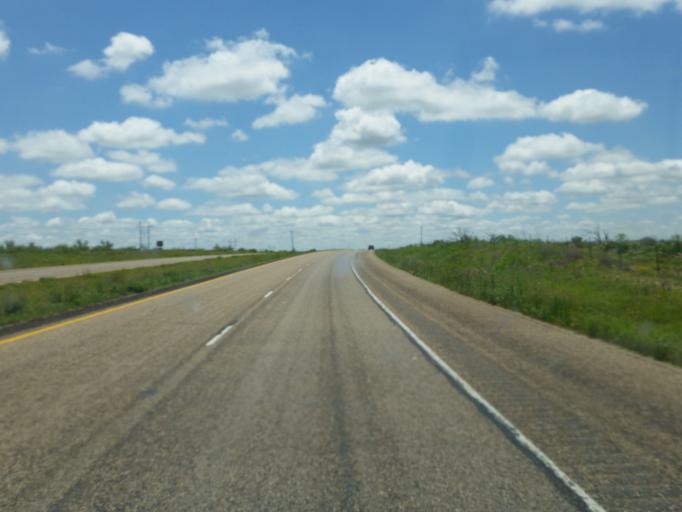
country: US
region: Texas
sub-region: Garza County
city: Post
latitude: 33.0933
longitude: -101.2483
